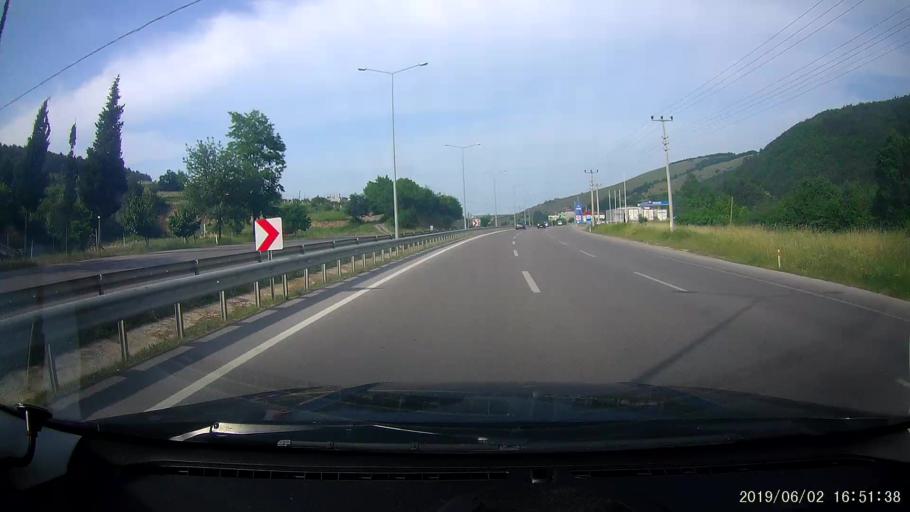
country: TR
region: Samsun
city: Taflan
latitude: 41.2765
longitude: 36.1853
